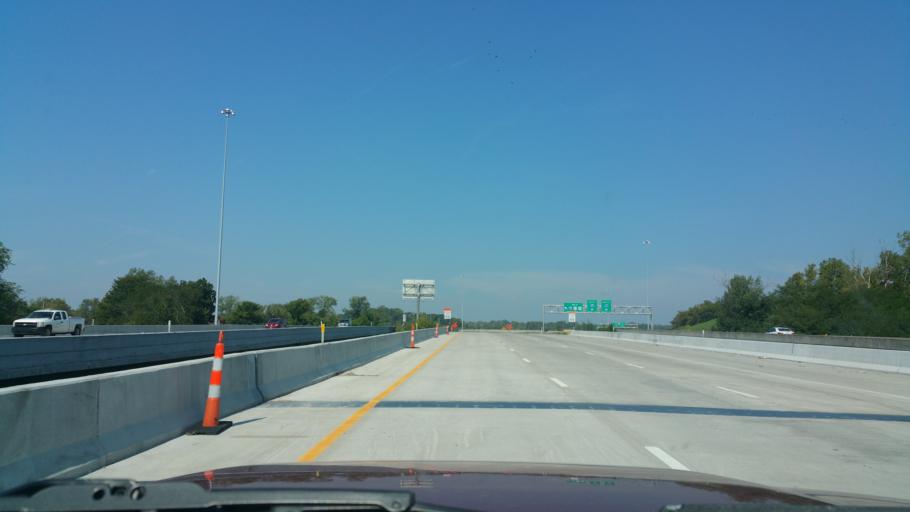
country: US
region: Kansas
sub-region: Wyandotte County
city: Kansas City
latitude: 39.1010
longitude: -94.6708
